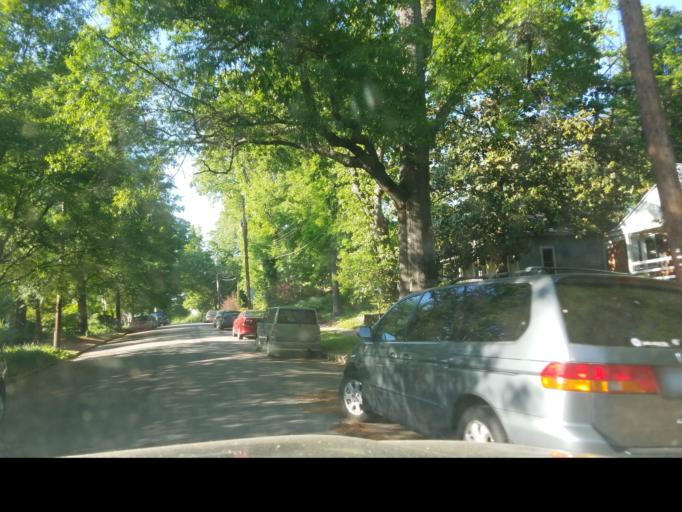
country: US
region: North Carolina
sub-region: Durham County
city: Durham
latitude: 36.0103
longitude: -78.9159
